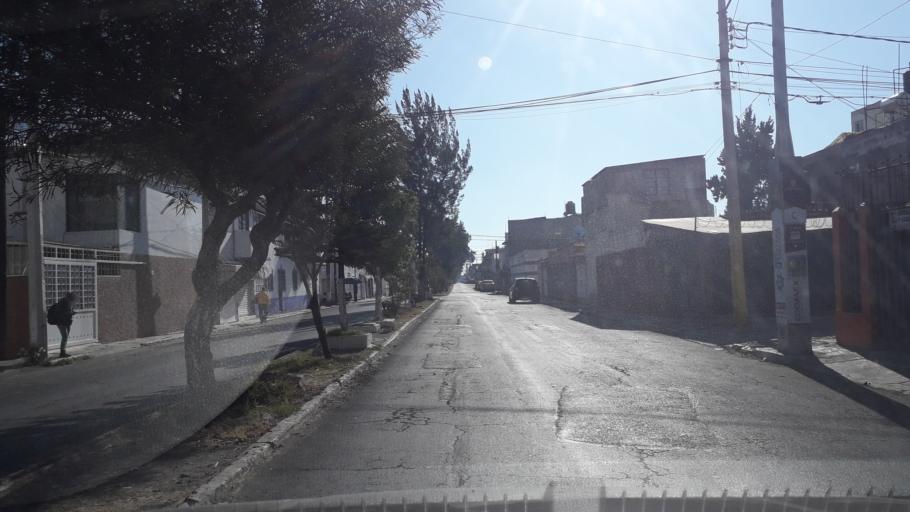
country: MX
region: Mexico City
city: Gustavo A. Madero
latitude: 19.5084
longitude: -99.0846
